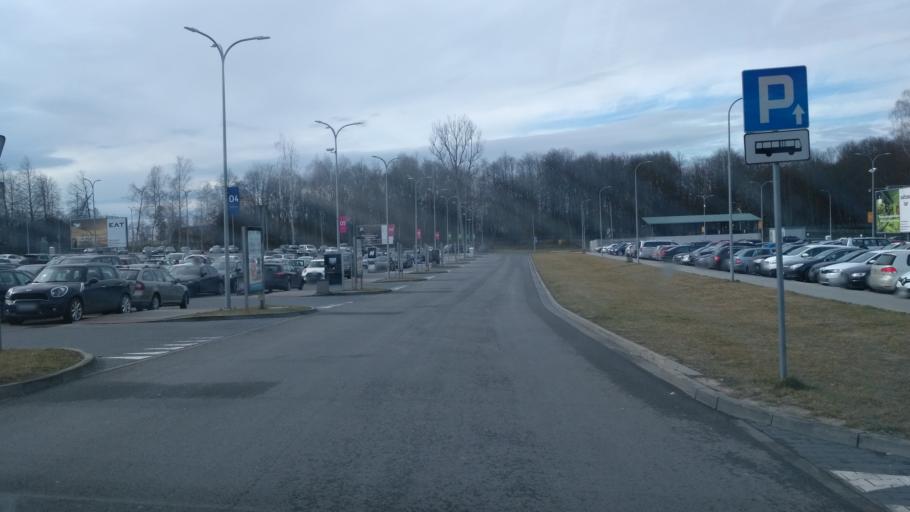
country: PL
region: Lesser Poland Voivodeship
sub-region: Powiat krakowski
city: Balice
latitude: 50.0714
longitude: 19.7993
